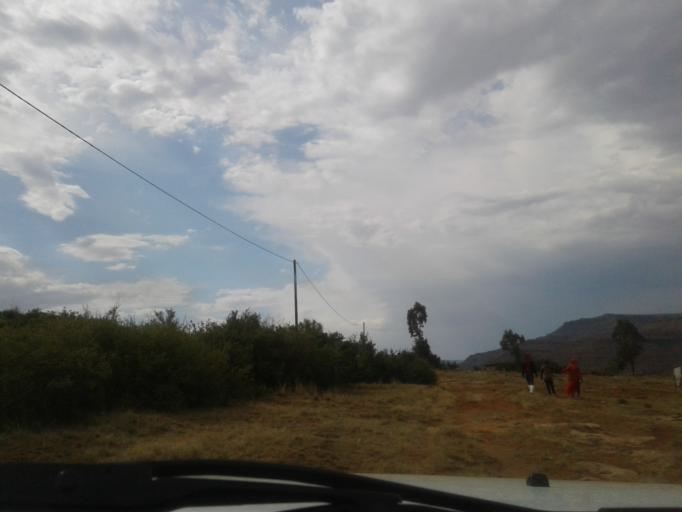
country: LS
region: Quthing
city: Quthing
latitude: -30.3761
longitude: 27.5556
